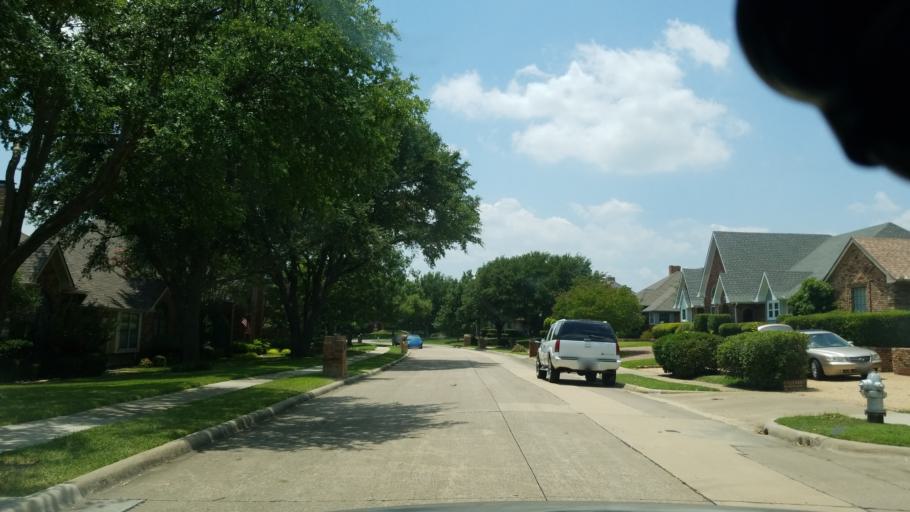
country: US
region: Texas
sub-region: Dallas County
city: Carrollton
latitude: 32.9694
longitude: -96.8796
